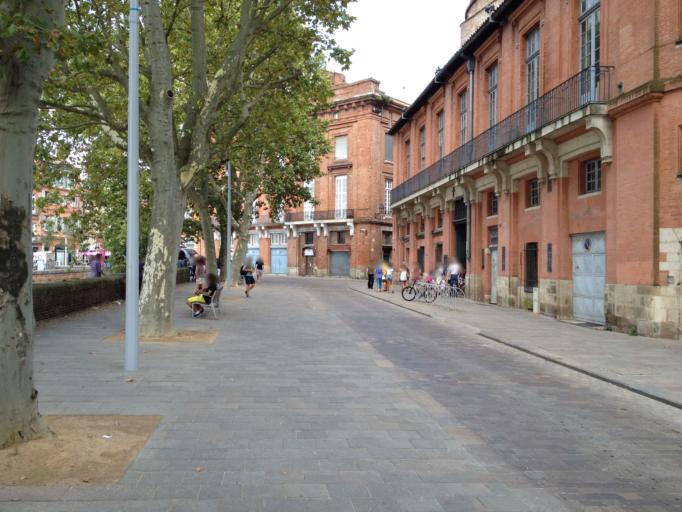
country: FR
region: Midi-Pyrenees
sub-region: Departement de la Haute-Garonne
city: Toulouse
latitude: 43.6010
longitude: 1.4393
